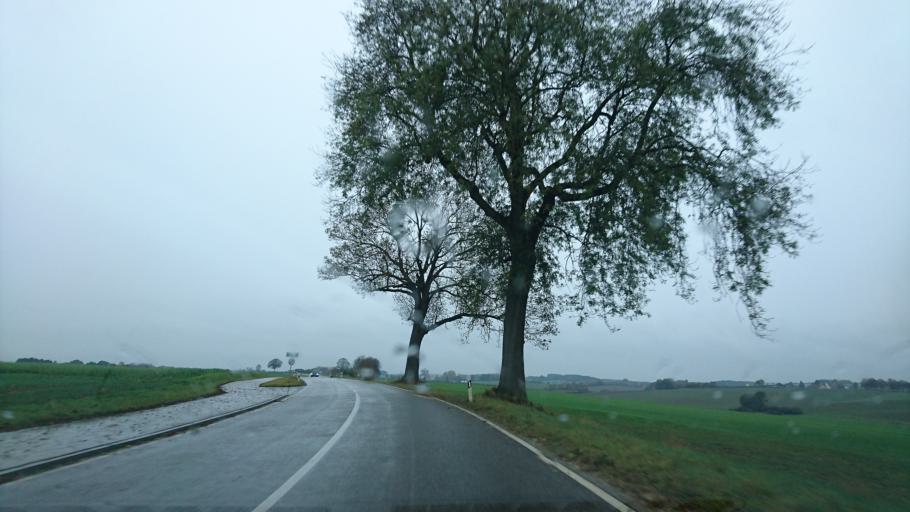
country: DE
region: Bavaria
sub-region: Upper Bavaria
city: Hilgertshausen-Tandern
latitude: 48.4319
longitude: 11.3414
